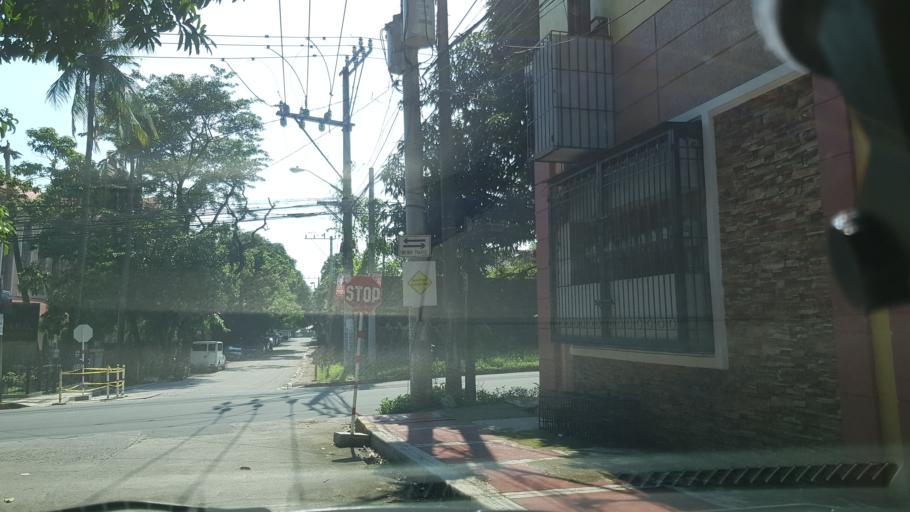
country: PH
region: Metro Manila
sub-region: San Juan
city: San Juan
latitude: 14.6151
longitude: 121.0312
